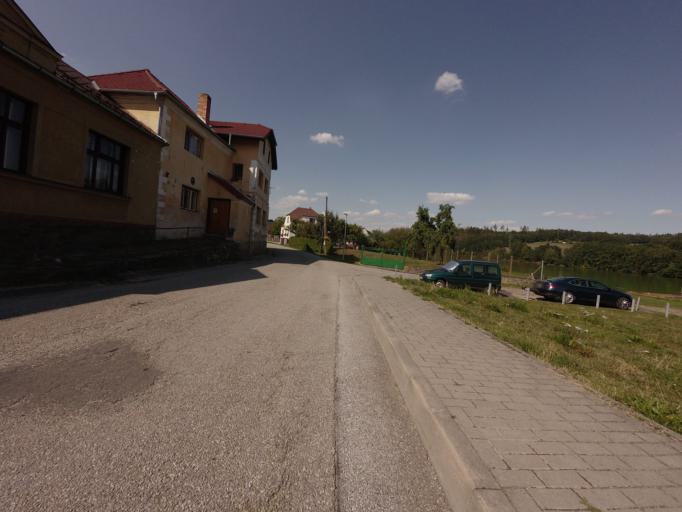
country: CZ
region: Jihocesky
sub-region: Okres Ceske Budejovice
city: Hluboka nad Vltavou
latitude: 49.1300
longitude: 14.4523
